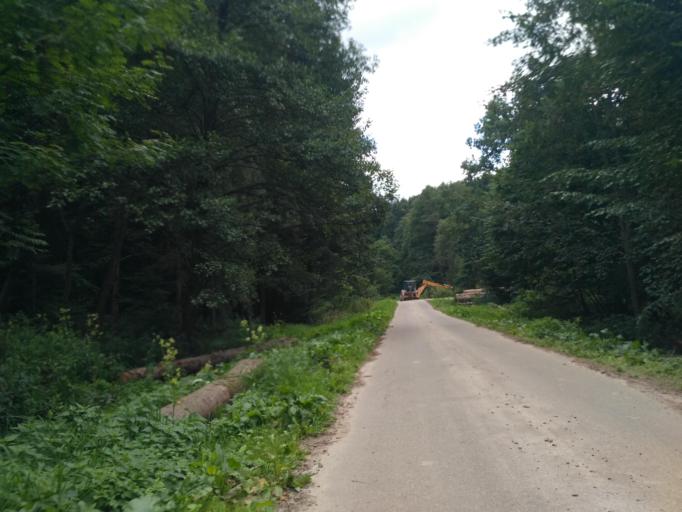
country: PL
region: Subcarpathian Voivodeship
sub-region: Powiat rzeszowski
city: Dynow
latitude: 49.7548
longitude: 22.2914
